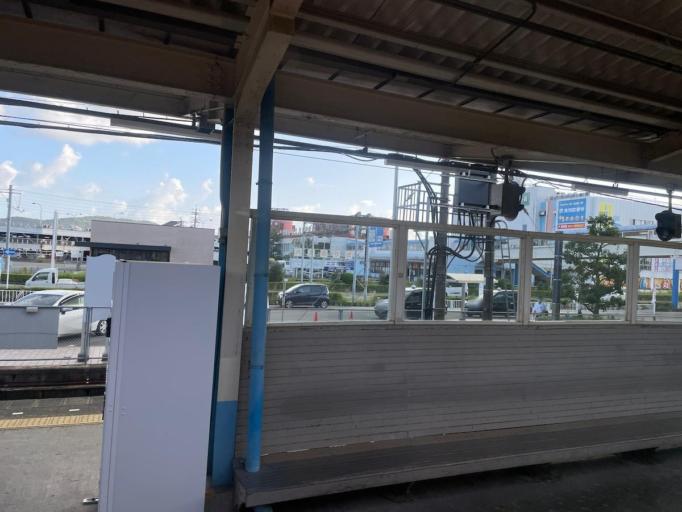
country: JP
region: Mie
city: Toba
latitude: 34.4870
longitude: 136.8426
